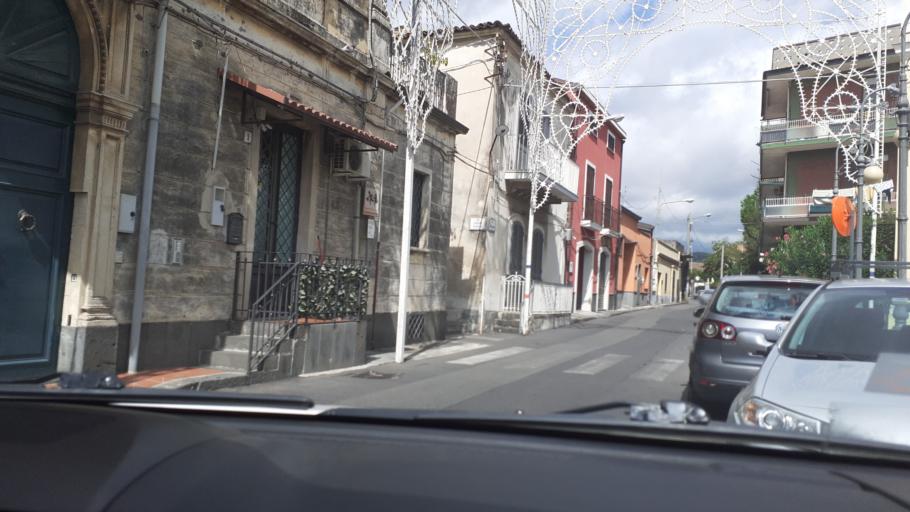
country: IT
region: Sicily
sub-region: Catania
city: San Giovanni la Punta
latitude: 37.5844
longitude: 15.0964
